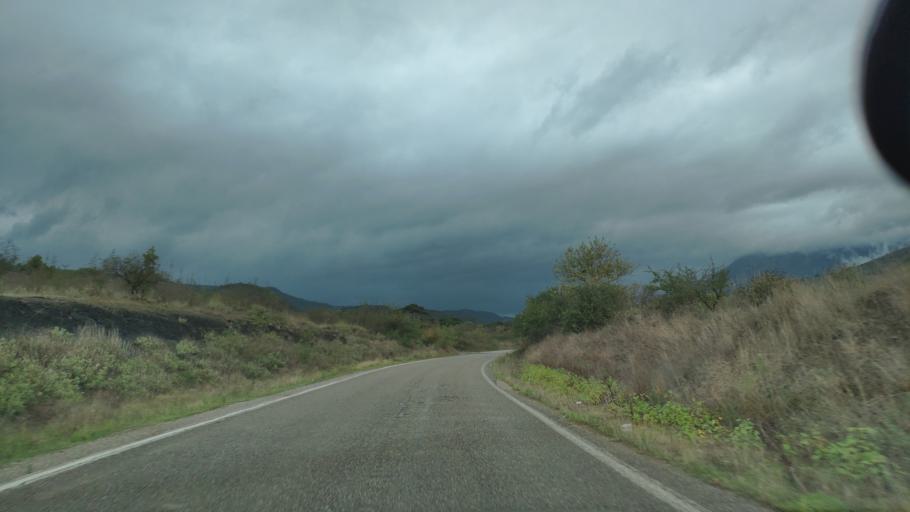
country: GR
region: West Greece
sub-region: Nomos Aitolias kai Akarnanias
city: Krikellos
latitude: 38.9789
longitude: 21.3240
